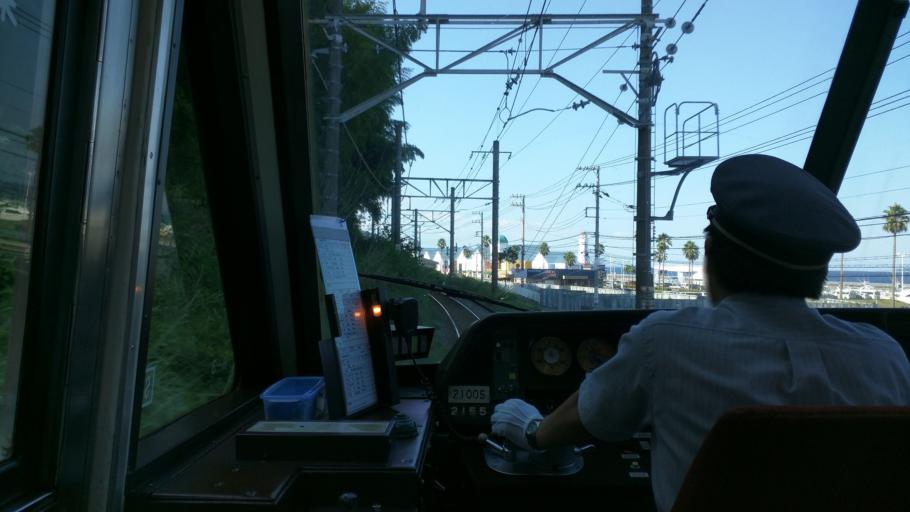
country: JP
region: Shizuoka
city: Ito
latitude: 34.9822
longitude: 139.0943
